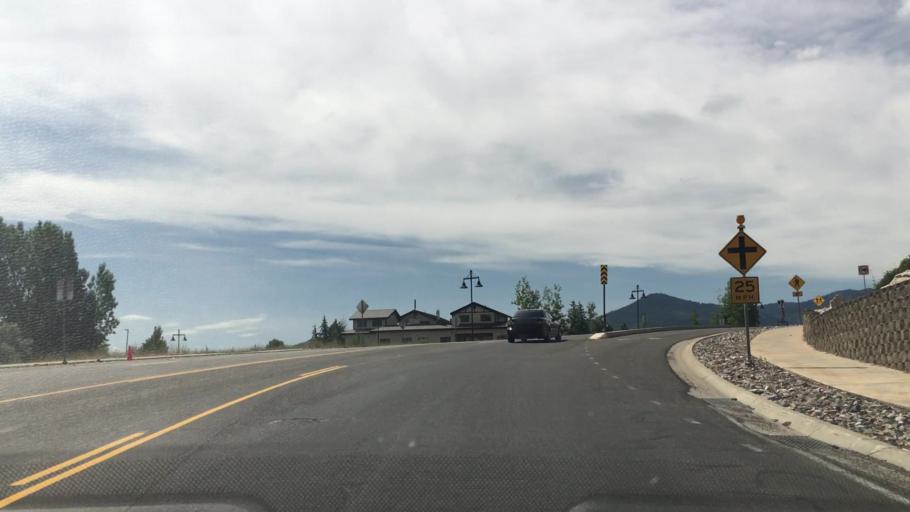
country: US
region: Utah
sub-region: Summit County
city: Snyderville
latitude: 40.7265
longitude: -111.5471
